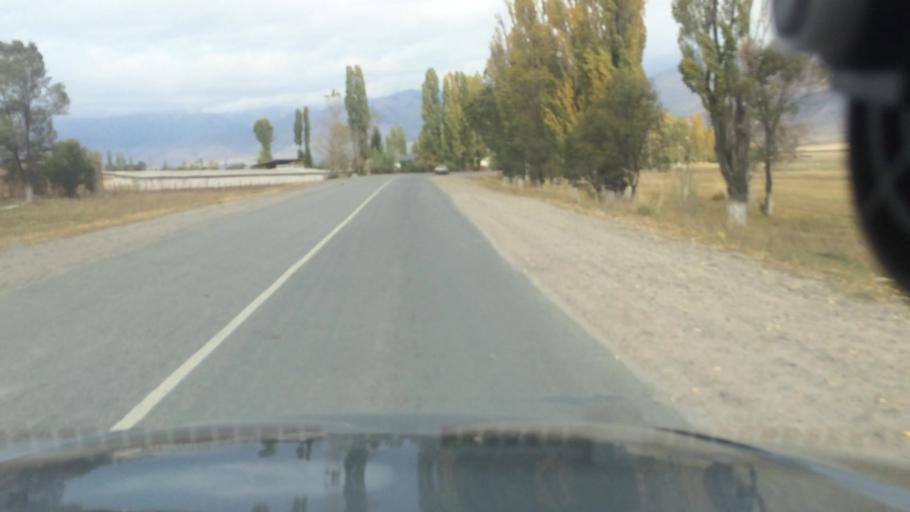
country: KG
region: Ysyk-Koel
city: Tyup
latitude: 42.7420
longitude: 78.3408
